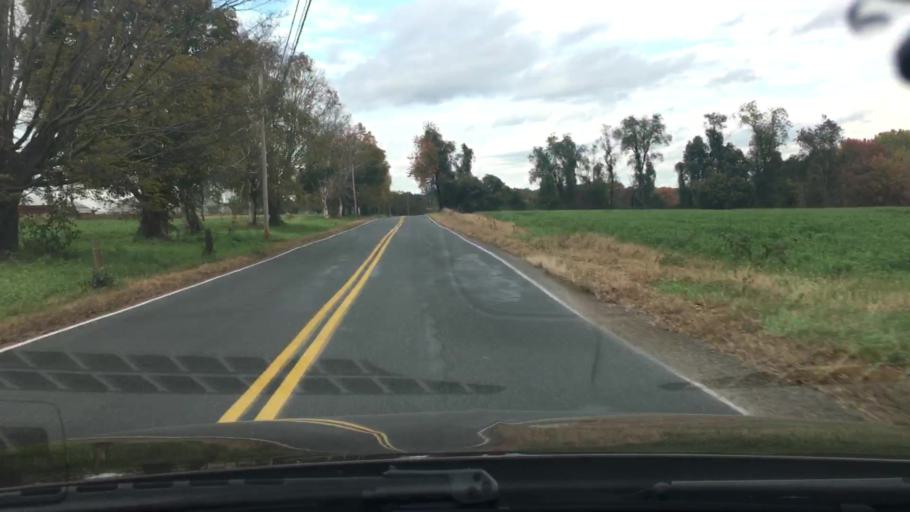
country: US
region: Connecticut
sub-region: Tolland County
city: Somers
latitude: 41.9556
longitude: -72.4826
